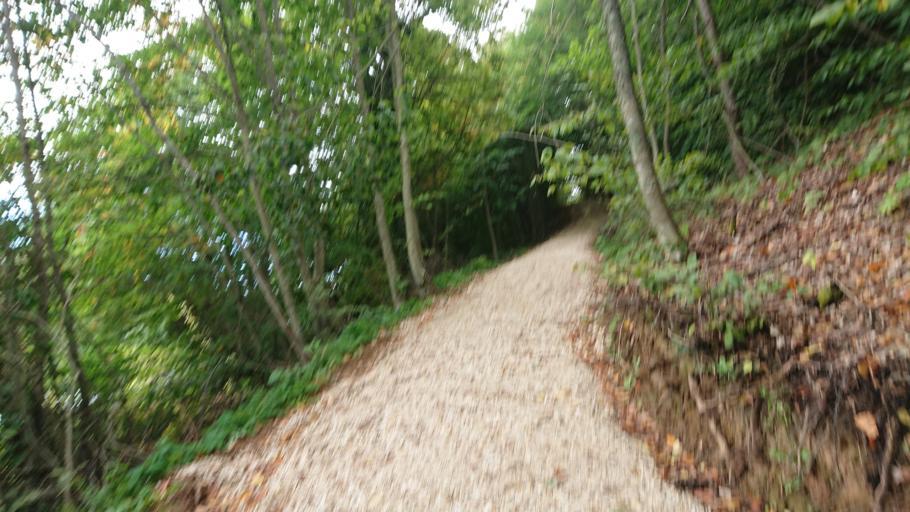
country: TR
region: Bilecik
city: Pazaryeri
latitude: 40.0173
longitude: 29.7900
